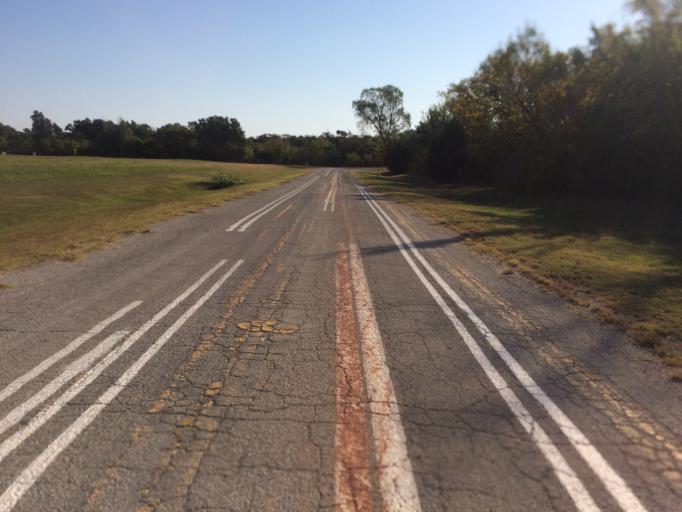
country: US
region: Oklahoma
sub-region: Cleveland County
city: Norman
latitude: 35.1809
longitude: -97.4340
